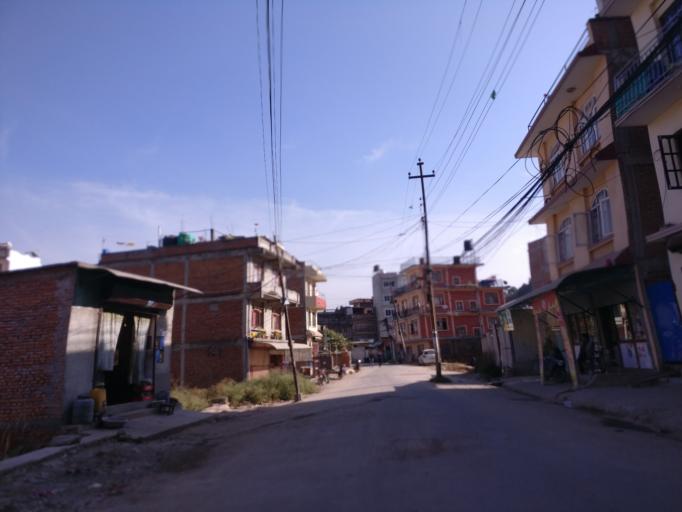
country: NP
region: Central Region
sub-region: Bagmati Zone
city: Patan
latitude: 27.6741
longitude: 85.3336
